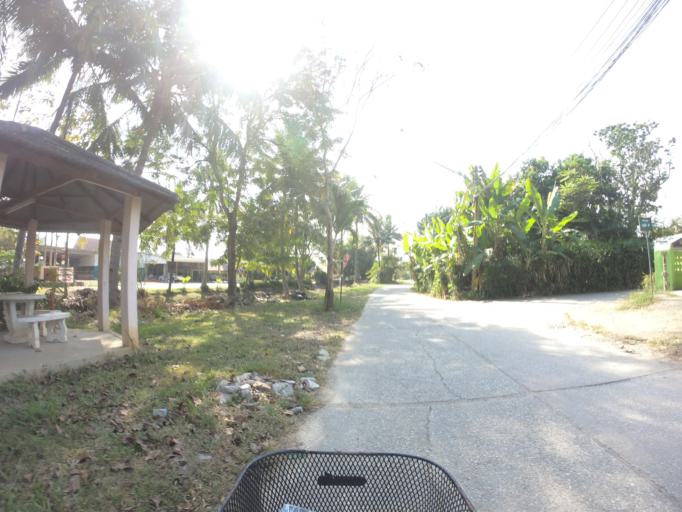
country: TH
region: Chiang Mai
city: Saraphi
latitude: 18.7088
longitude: 99.0600
